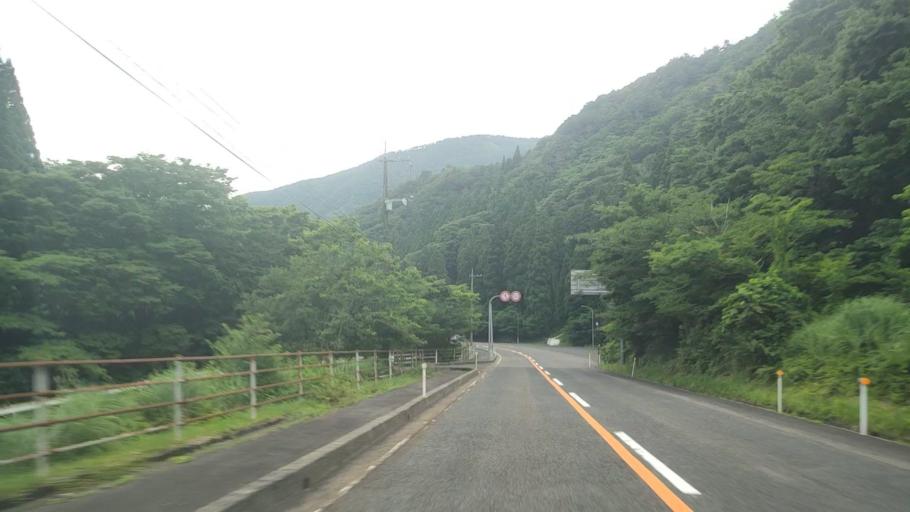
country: JP
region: Tottori
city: Kurayoshi
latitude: 35.3170
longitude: 133.8983
